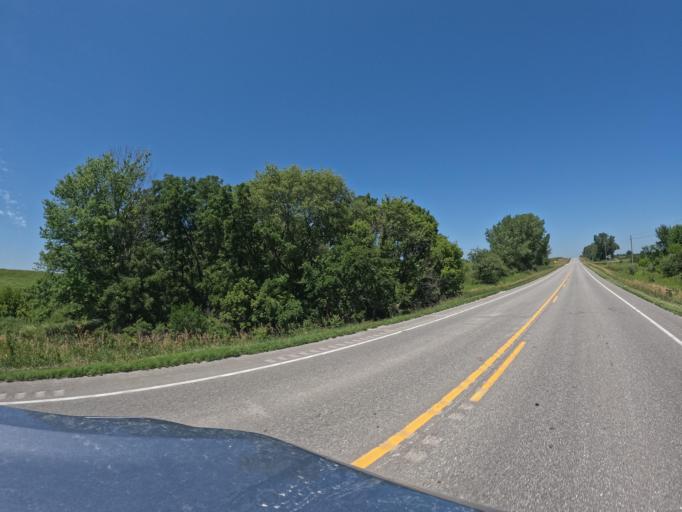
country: US
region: Iowa
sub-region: Keokuk County
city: Sigourney
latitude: 41.4648
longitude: -92.3552
